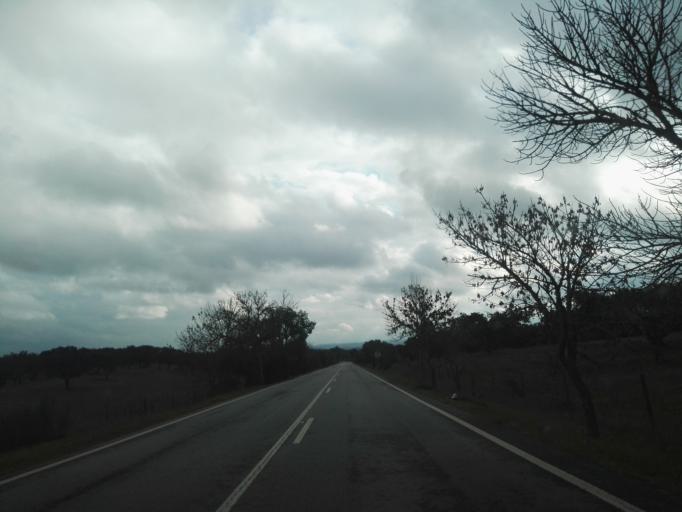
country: PT
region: Portalegre
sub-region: Arronches
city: Arronches
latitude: 39.0783
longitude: -7.2798
